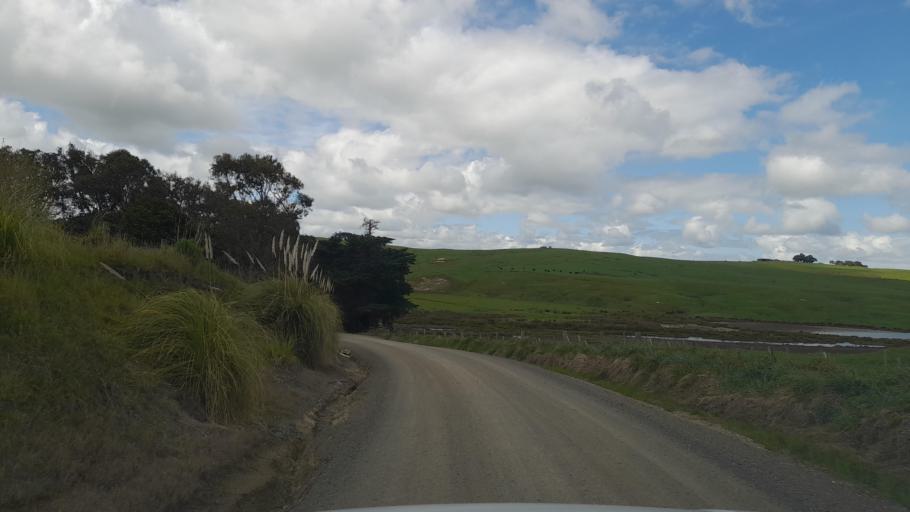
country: NZ
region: Auckland
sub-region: Auckland
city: Wellsford
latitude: -36.1926
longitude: 174.3267
